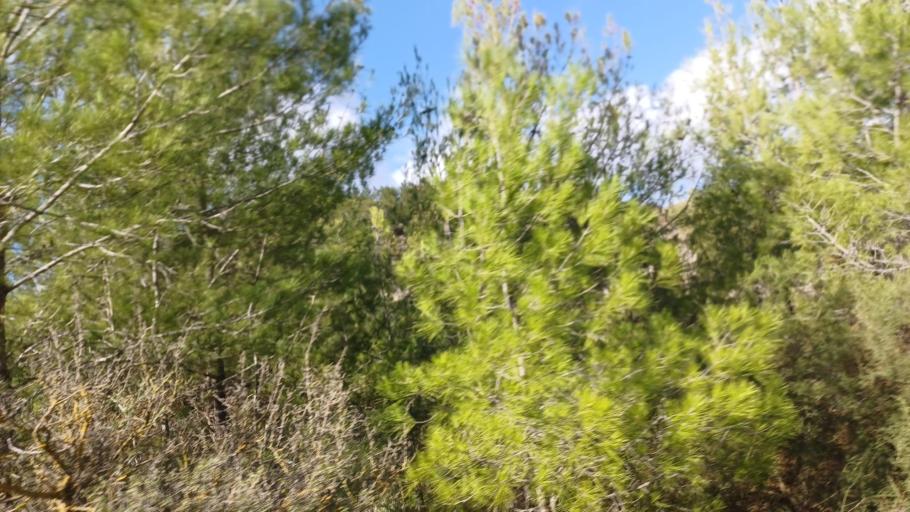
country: CY
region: Limassol
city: Pachna
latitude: 34.8513
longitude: 32.6873
